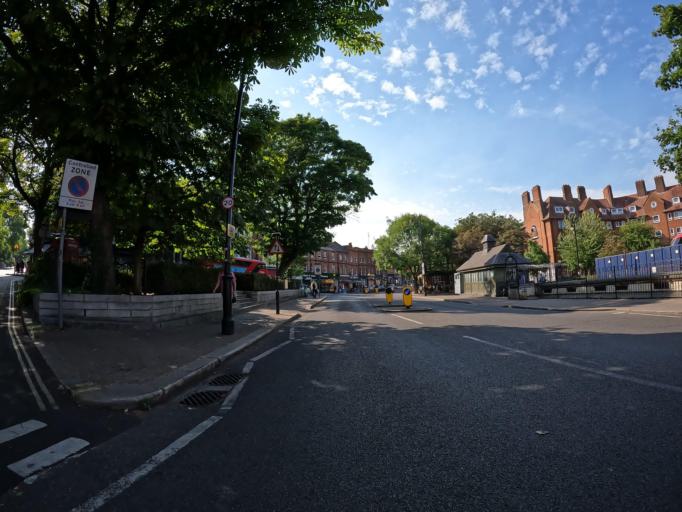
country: GB
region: England
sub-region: Greater London
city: Hendon
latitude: 51.6093
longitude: -0.2198
